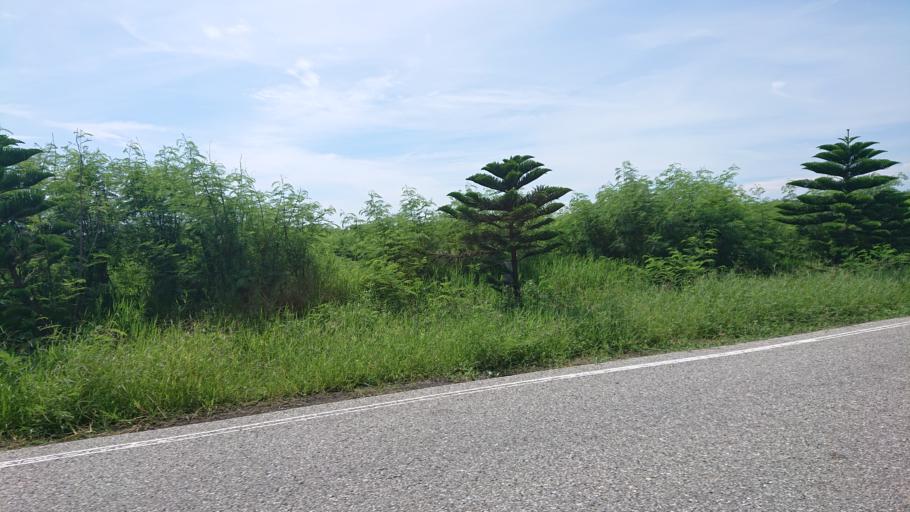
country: TW
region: Taiwan
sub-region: Penghu
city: Ma-kung
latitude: 23.6421
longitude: 119.5163
